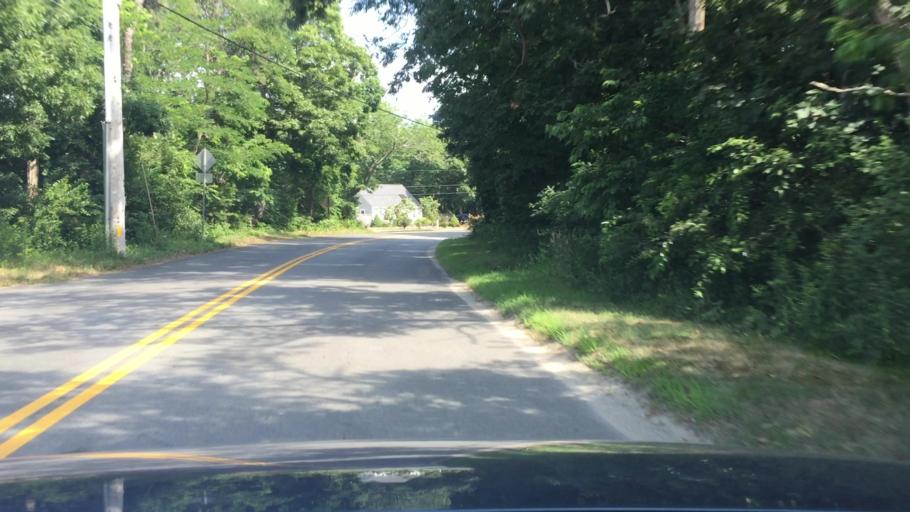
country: US
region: Massachusetts
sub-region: Barnstable County
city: North Eastham
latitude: 41.8645
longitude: -69.9824
